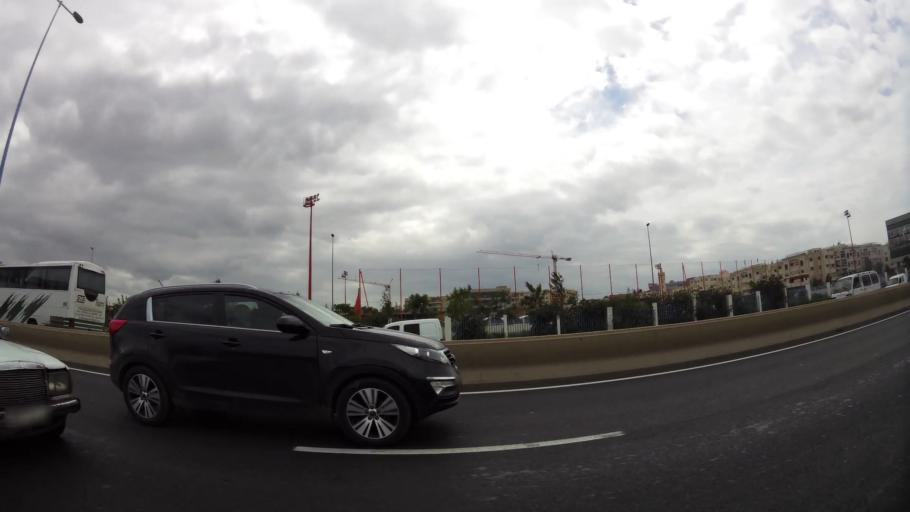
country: MA
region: Grand Casablanca
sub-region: Casablanca
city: Casablanca
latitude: 33.5506
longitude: -7.6378
